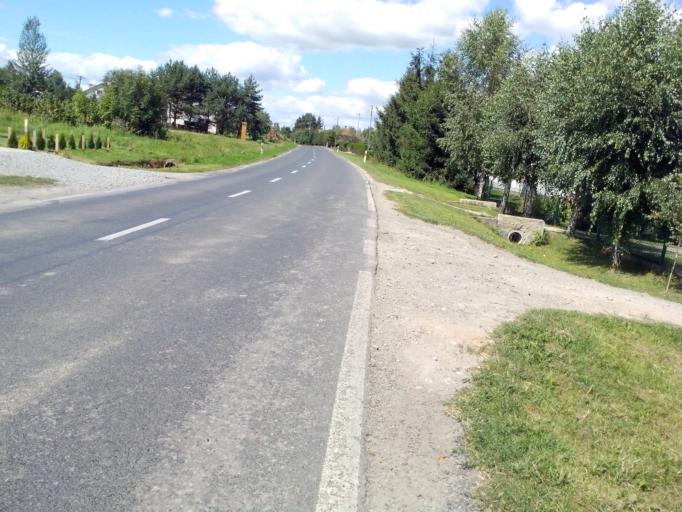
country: PL
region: Subcarpathian Voivodeship
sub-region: Powiat strzyzowski
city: Strzyzow
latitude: 49.8374
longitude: 21.8238
